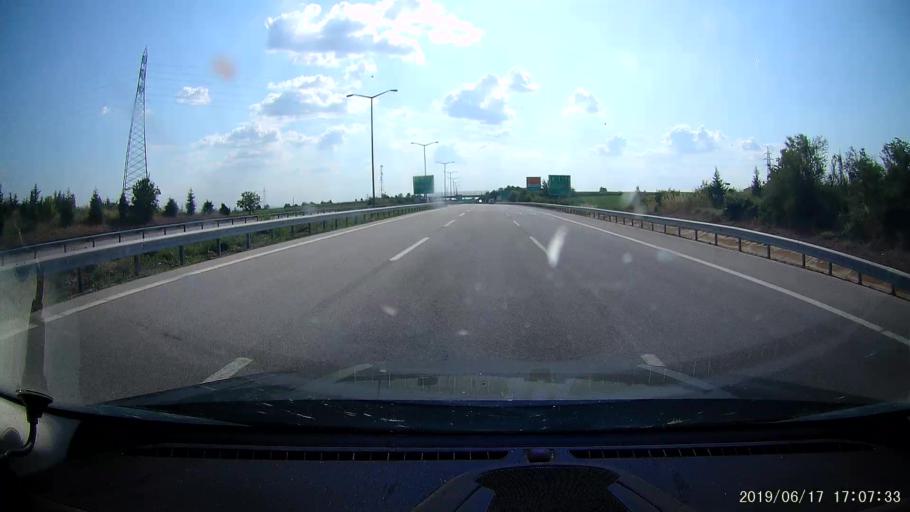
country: TR
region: Edirne
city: Edirne
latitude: 41.6617
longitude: 26.6378
